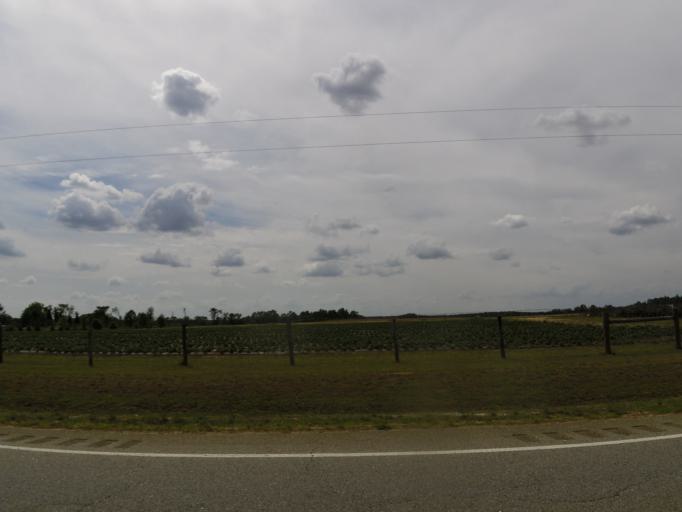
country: US
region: Georgia
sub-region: Jefferson County
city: Louisville
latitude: 33.0776
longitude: -82.4046
